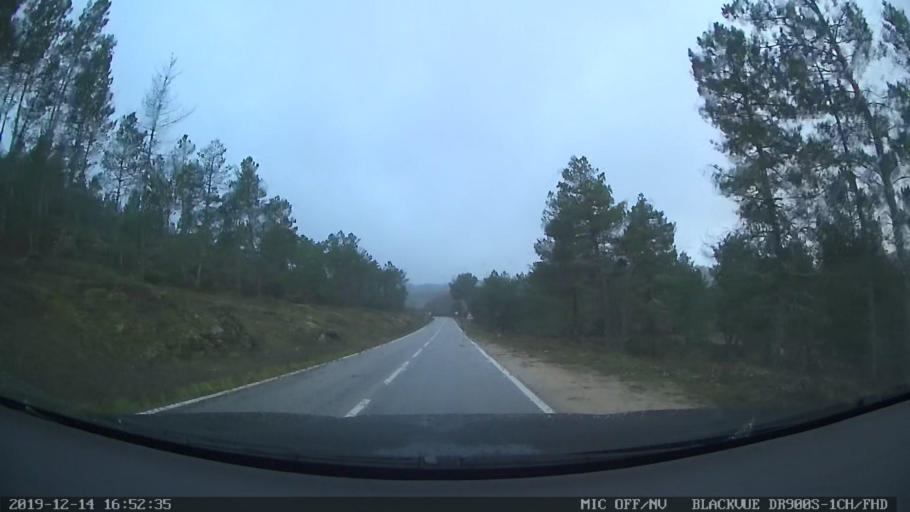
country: PT
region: Vila Real
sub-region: Murca
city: Murca
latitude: 41.4270
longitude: -7.5109
